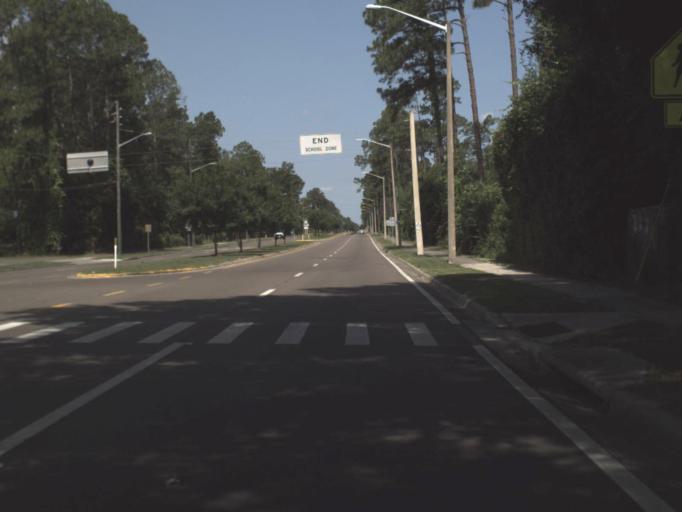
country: US
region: Florida
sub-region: Alachua County
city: Gainesville
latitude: 29.6519
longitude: -82.2722
